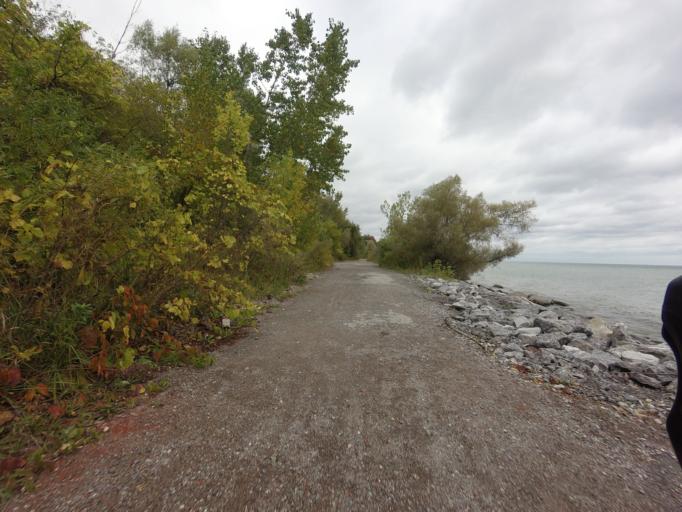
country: CA
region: Ontario
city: Scarborough
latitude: 43.7443
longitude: -79.1920
